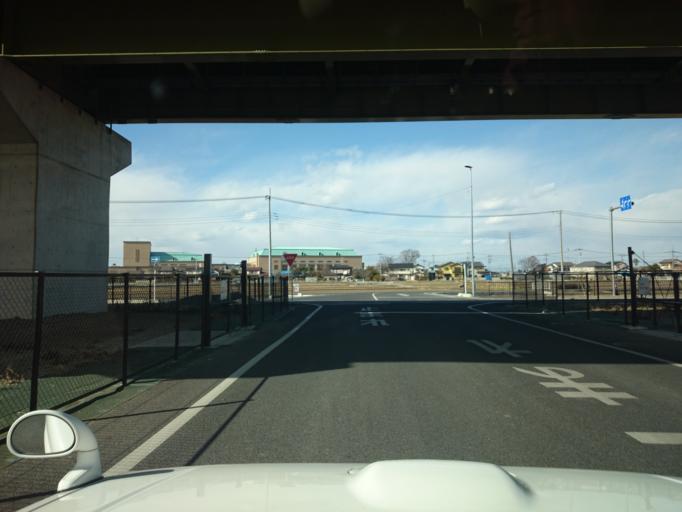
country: JP
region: Saitama
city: Satte
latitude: 36.0649
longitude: 139.7393
